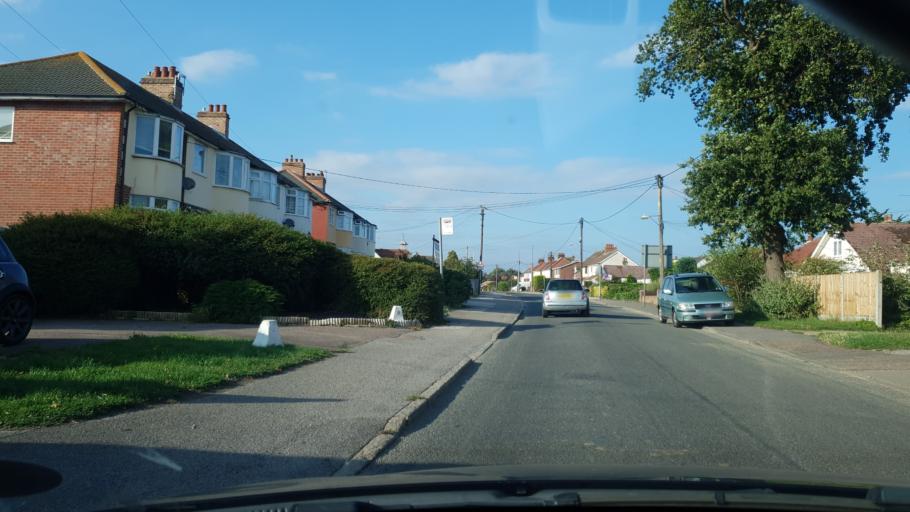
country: GB
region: England
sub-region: Essex
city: Frinton-on-Sea
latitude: 51.8426
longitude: 1.2199
